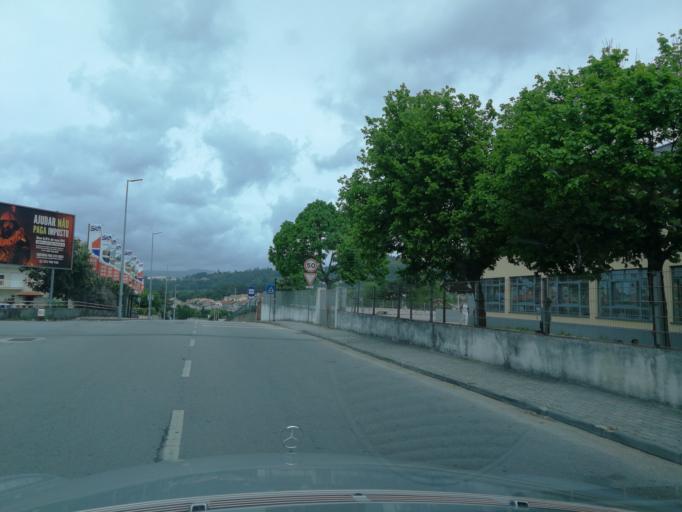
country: PT
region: Braga
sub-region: Amares
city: Amares
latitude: 41.6264
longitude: -8.3691
